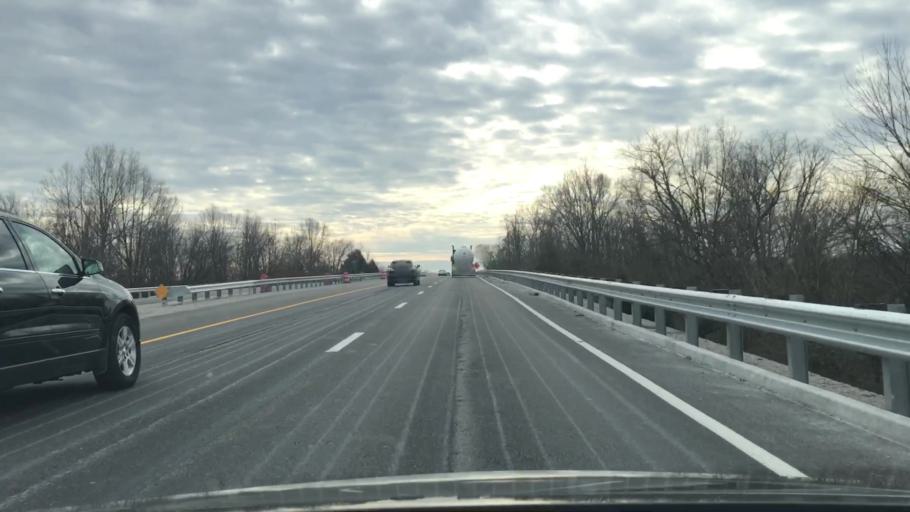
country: US
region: Kentucky
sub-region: Ohio County
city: Oak Grove
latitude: 37.2855
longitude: -86.7428
